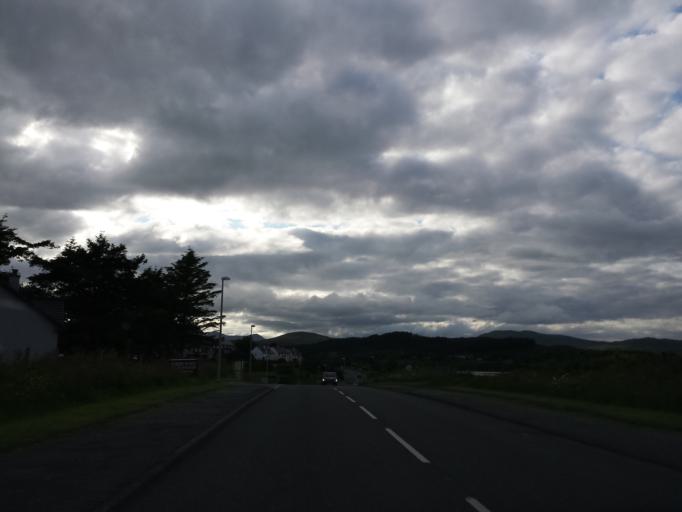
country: GB
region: Scotland
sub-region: Highland
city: Portree
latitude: 57.2383
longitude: -5.8962
